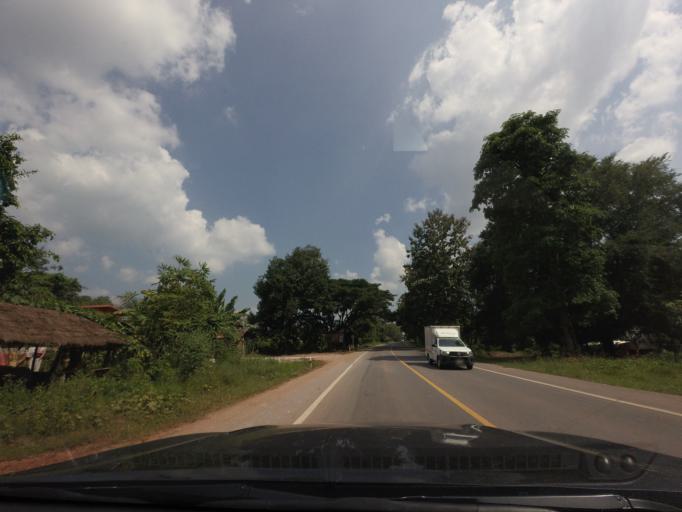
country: TH
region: Phitsanulok
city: Chat Trakan
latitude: 17.2913
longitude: 100.5143
